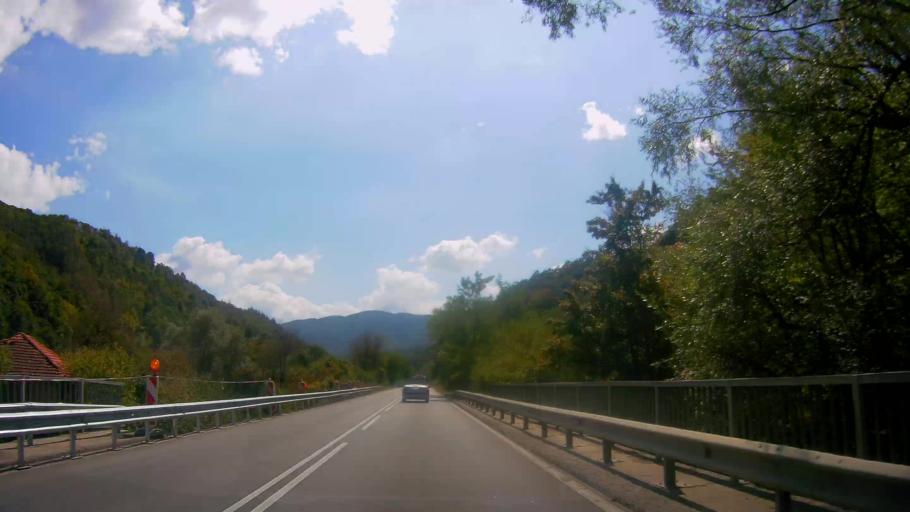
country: BG
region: Stara Zagora
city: Gurkovo
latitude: 42.7319
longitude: 25.7121
